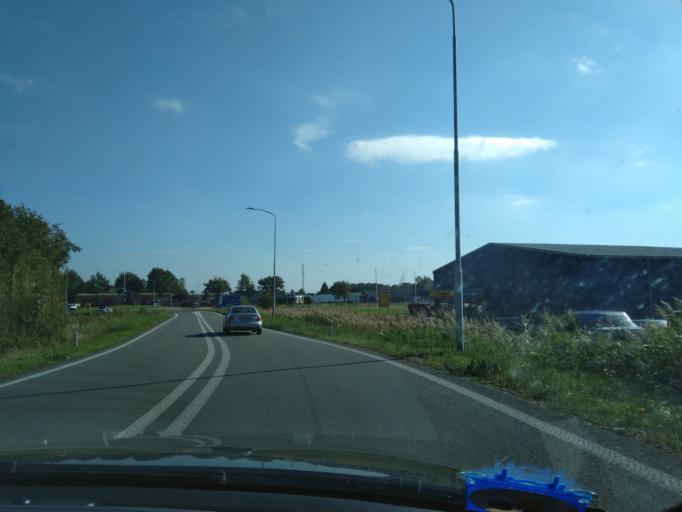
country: NL
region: Groningen
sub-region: Gemeente Pekela
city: Oude Pekela
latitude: 53.0864
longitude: 6.9633
